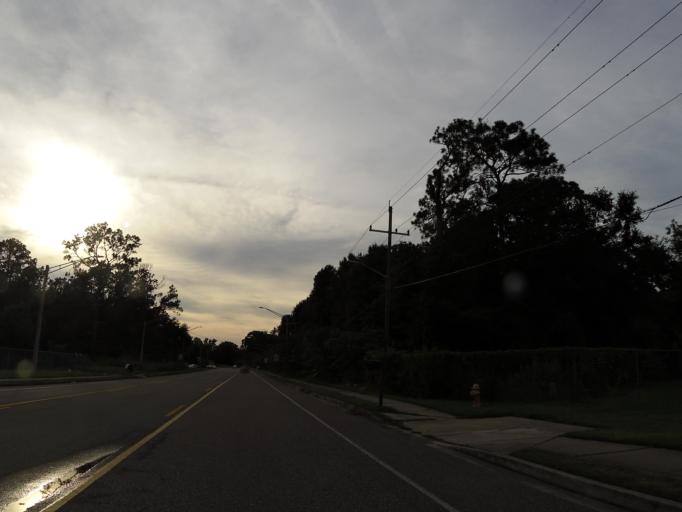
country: US
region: Florida
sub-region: Duval County
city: Jacksonville
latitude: 30.3931
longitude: -81.7330
